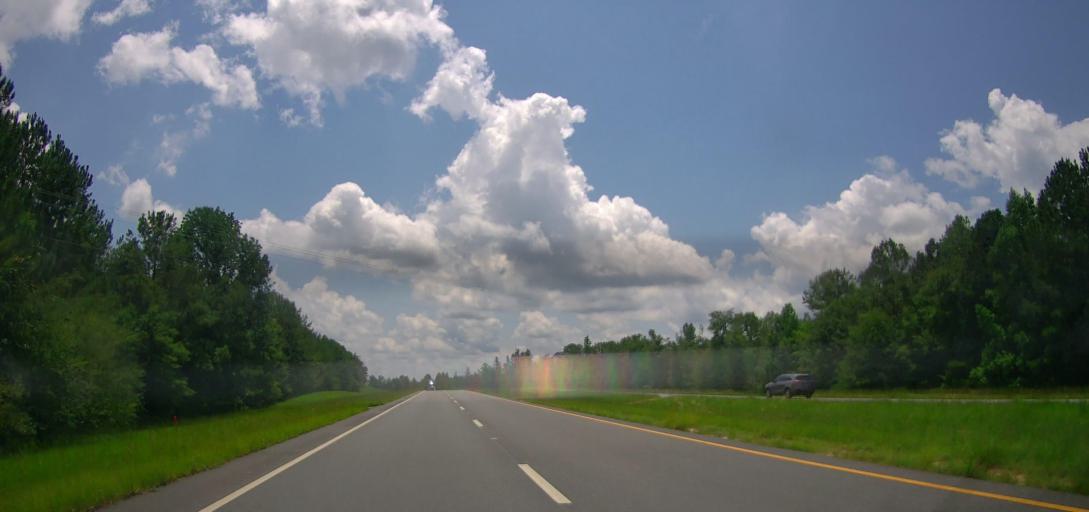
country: US
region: Georgia
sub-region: Upson County
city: Thomaston
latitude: 32.7579
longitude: -84.2442
